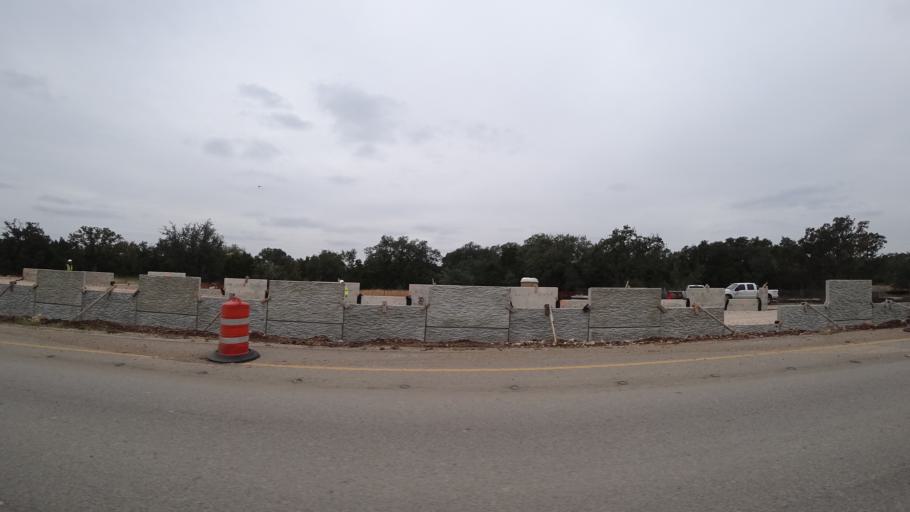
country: US
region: Texas
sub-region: Travis County
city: Shady Hollow
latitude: 30.1754
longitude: -97.8898
